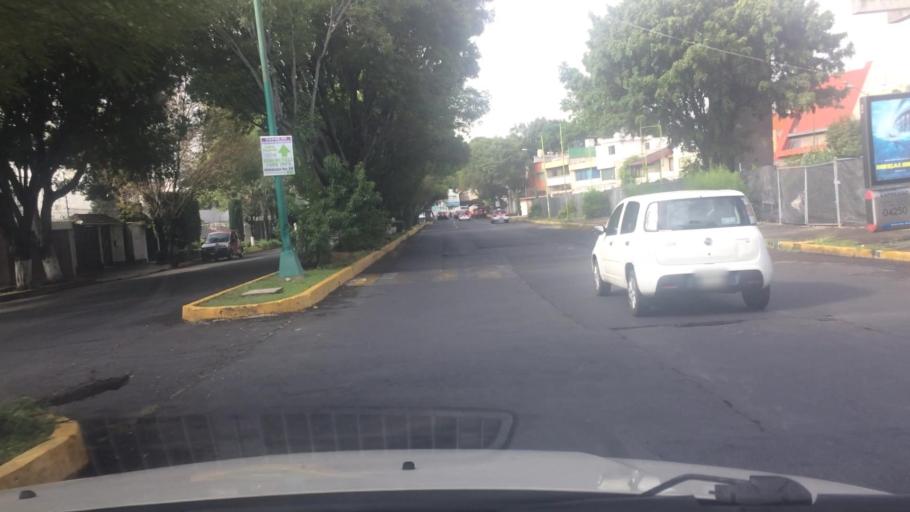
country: MX
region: Mexico City
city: Coyoacan
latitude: 19.3405
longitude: -99.1272
